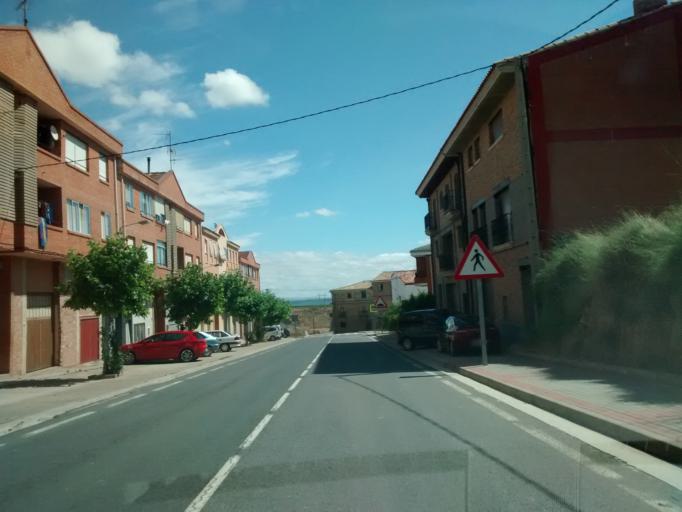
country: ES
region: La Rioja
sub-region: Provincia de La Rioja
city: Leza de Rio Leza
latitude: 42.3574
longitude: -2.3876
